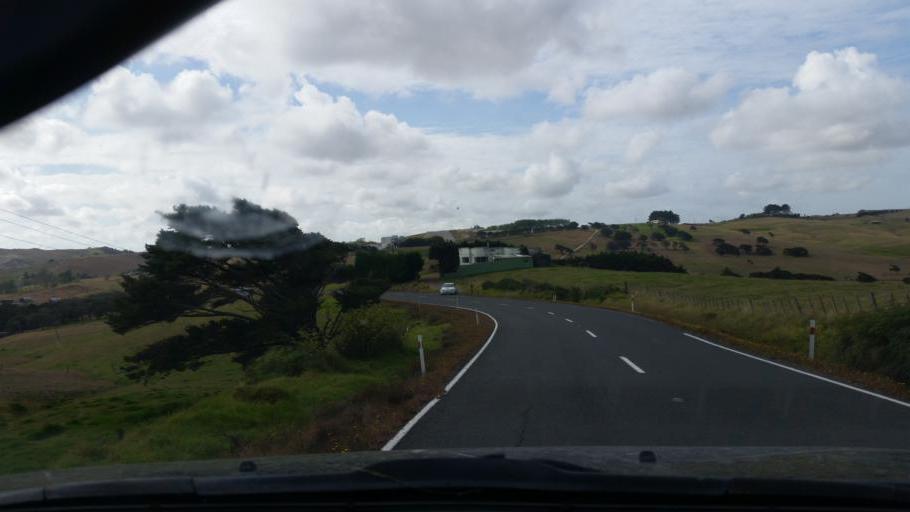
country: NZ
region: Northland
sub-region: Kaipara District
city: Dargaville
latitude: -35.9641
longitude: 173.9297
